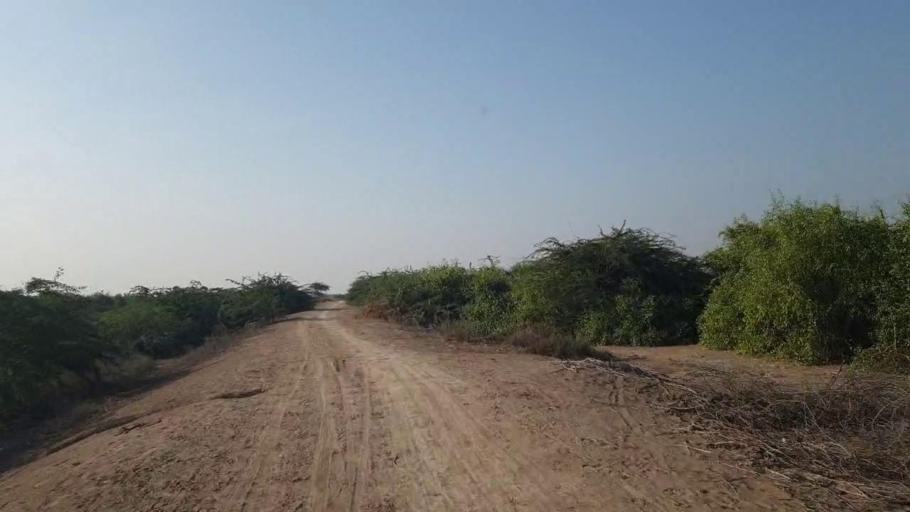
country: PK
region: Sindh
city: Badin
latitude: 24.4683
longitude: 68.7394
